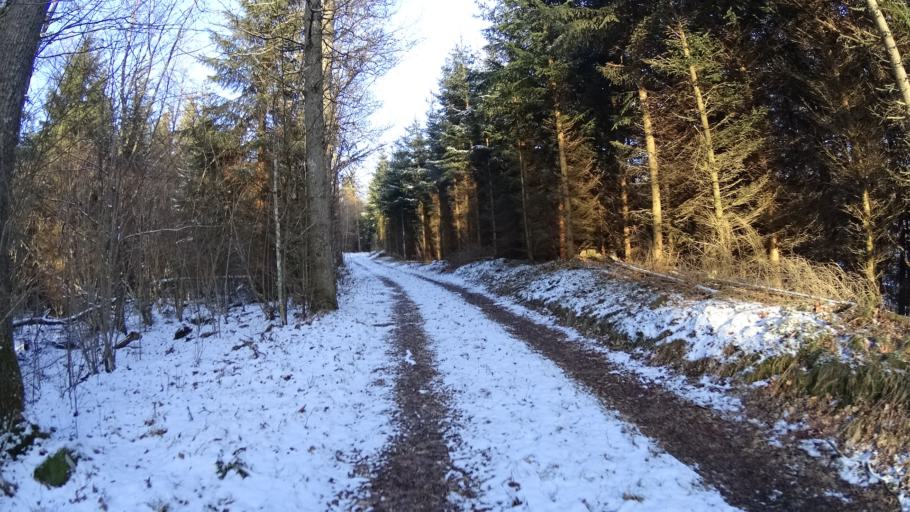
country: SE
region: Skane
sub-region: Hoors Kommun
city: Hoeoer
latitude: 55.9935
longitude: 13.5554
